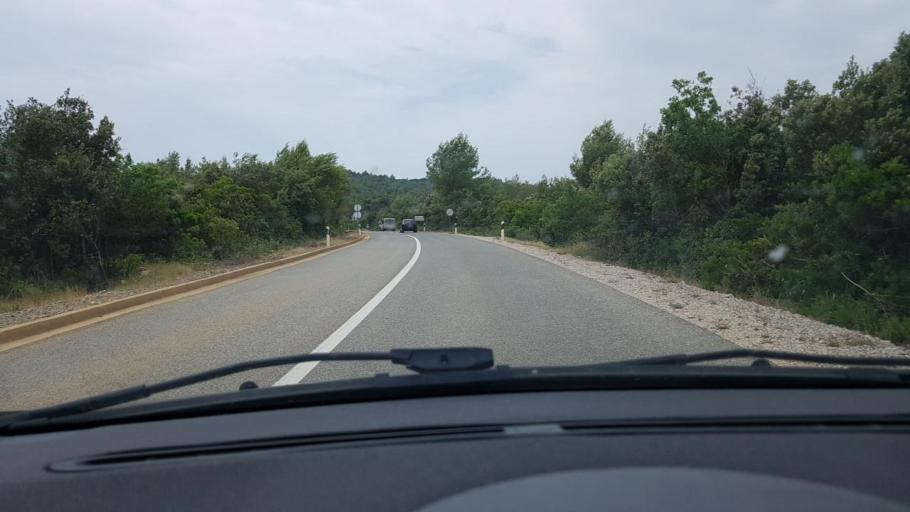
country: HR
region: Dubrovacko-Neretvanska
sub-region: Grad Korcula
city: Zrnovo
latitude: 42.9372
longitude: 17.0859
